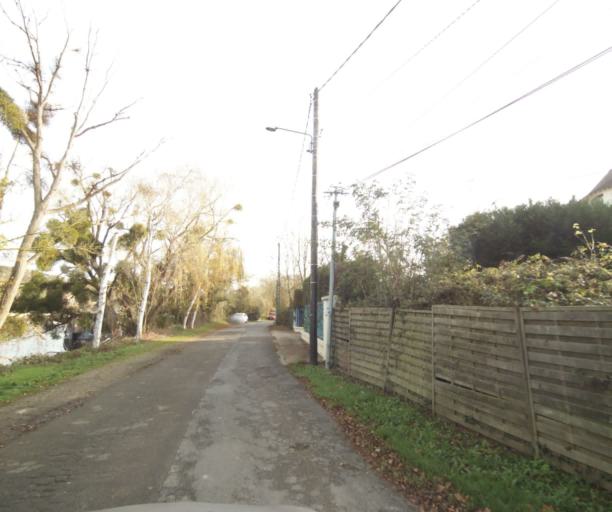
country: FR
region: Ile-de-France
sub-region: Departement du Val-d'Oise
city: Herblay
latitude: 48.9830
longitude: 2.1690
